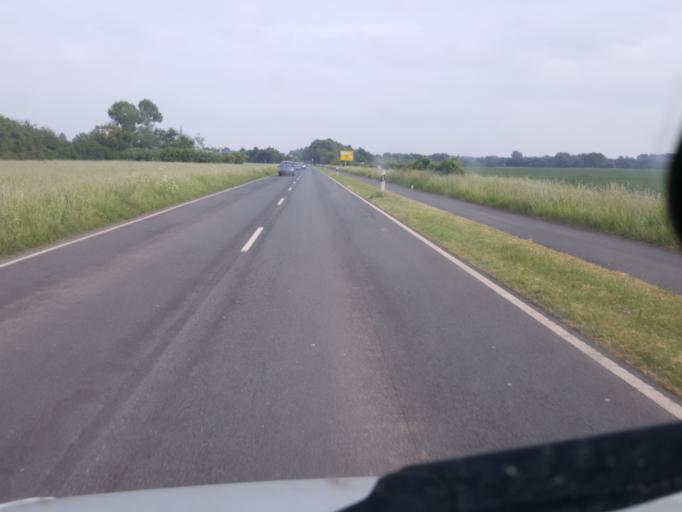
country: DE
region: Lower Saxony
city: Nienburg
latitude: 52.6486
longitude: 9.1928
